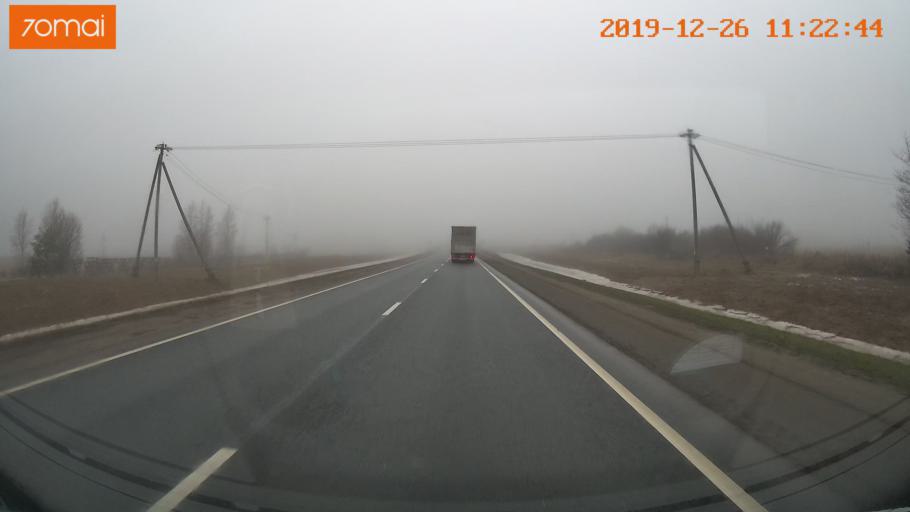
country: RU
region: Vologda
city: Chebsara
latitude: 59.1296
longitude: 38.9368
